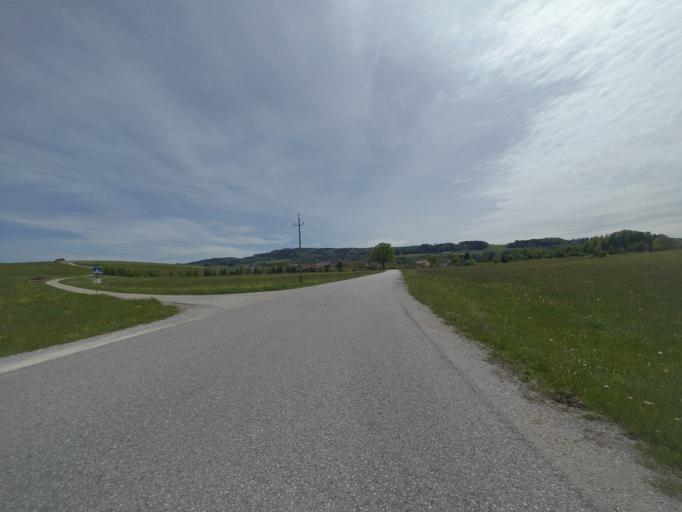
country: AT
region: Salzburg
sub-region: Politischer Bezirk Salzburg-Umgebung
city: Mattsee
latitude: 47.9942
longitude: 13.1264
